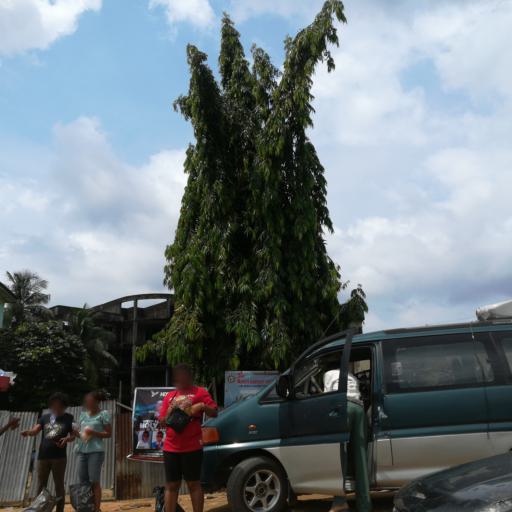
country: NG
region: Rivers
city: Port Harcourt
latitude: 4.8511
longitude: 7.0630
